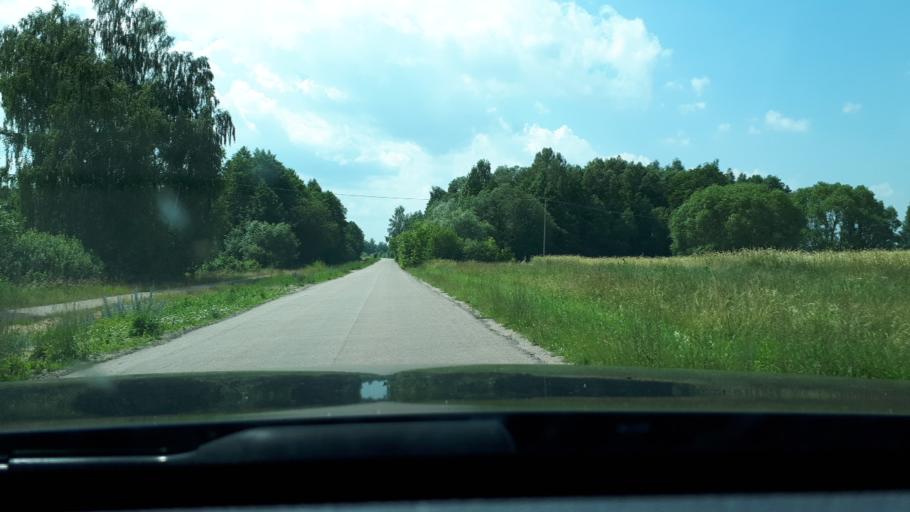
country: PL
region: Podlasie
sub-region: Powiat bialostocki
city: Choroszcz
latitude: 53.1213
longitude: 22.9072
